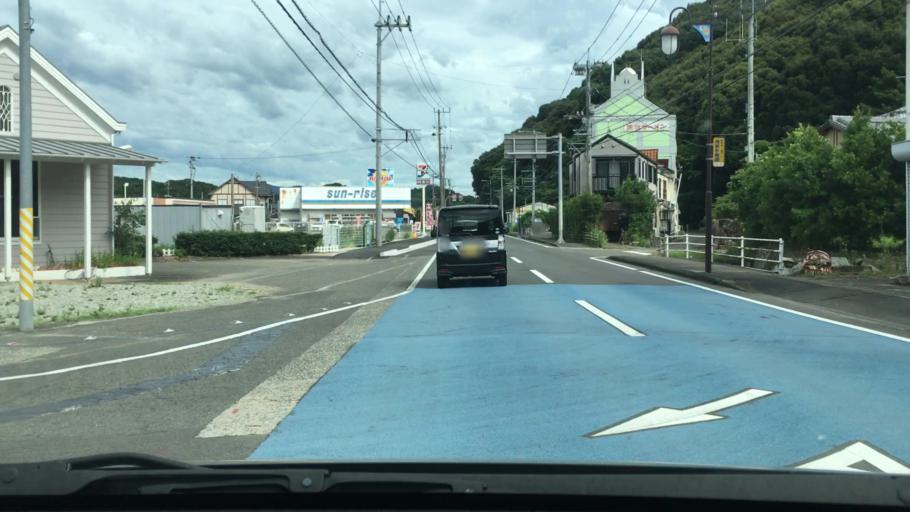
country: JP
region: Nagasaki
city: Togitsu
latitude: 32.8887
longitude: 129.7865
